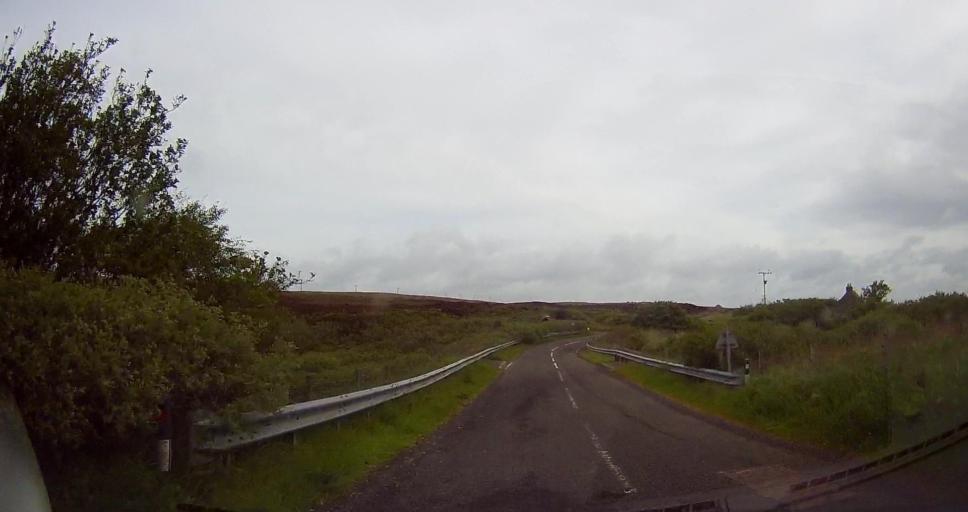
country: GB
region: Scotland
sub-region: Orkney Islands
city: Stromness
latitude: 58.8399
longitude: -3.2168
